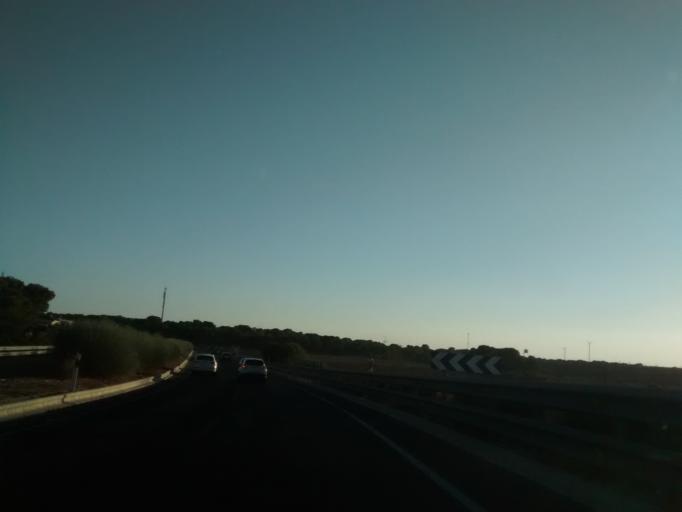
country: ES
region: Valencia
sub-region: Provincia de Alicante
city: Pilar de la Horadada
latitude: 37.8907
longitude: -0.7655
